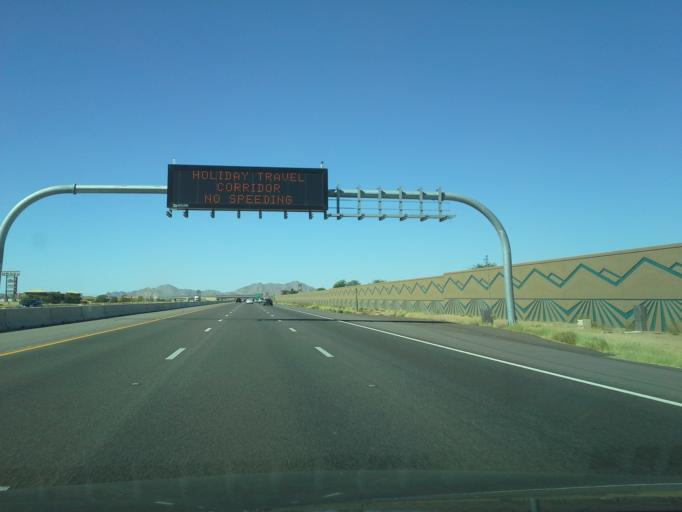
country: US
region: Arizona
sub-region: Pinal County
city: Casa Grande
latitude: 32.8691
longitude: -111.6869
